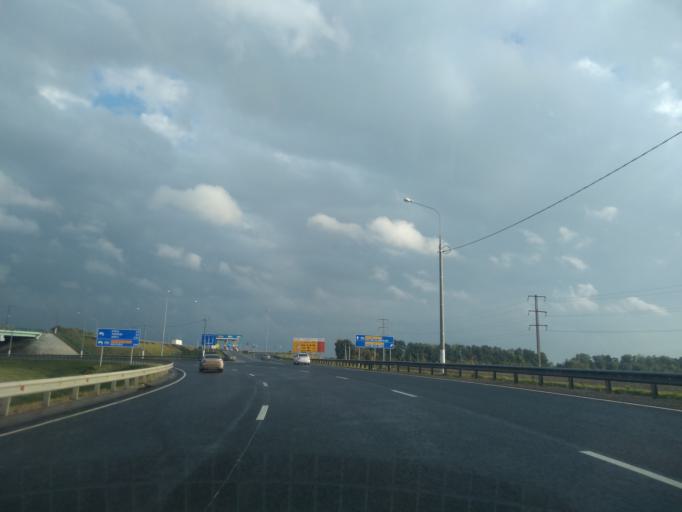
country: RU
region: Lipetsk
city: Yelets
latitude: 52.5450
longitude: 38.7173
